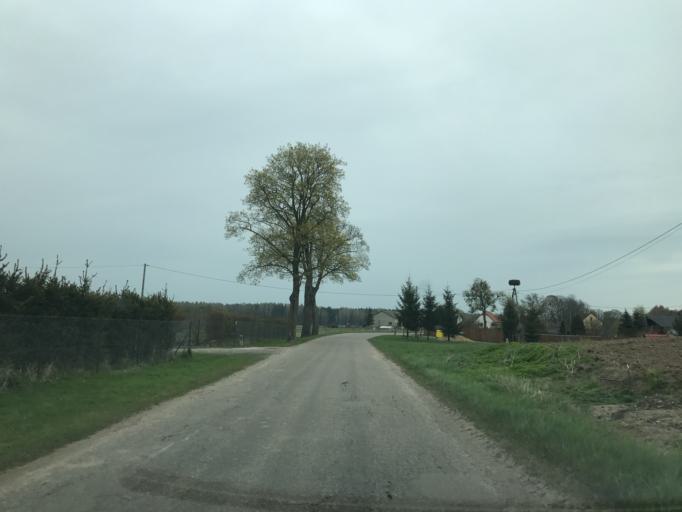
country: PL
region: Warmian-Masurian Voivodeship
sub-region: Powiat olsztynski
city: Olsztynek
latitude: 53.6322
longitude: 20.1780
